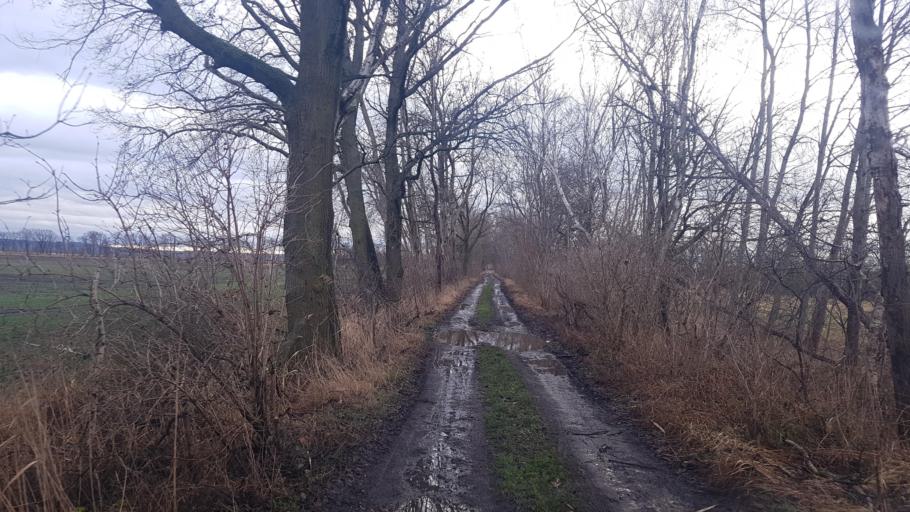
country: DE
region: Brandenburg
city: Plessa
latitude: 51.4320
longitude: 13.6496
